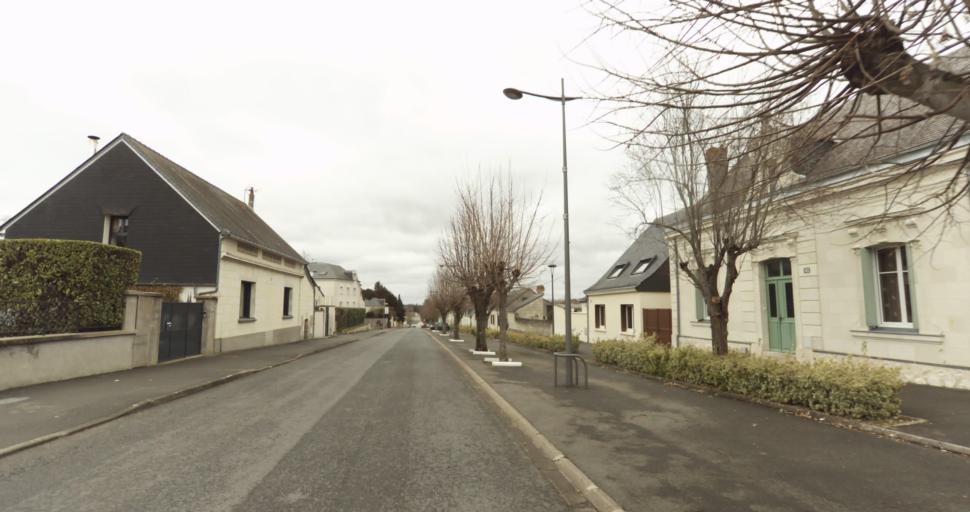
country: FR
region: Pays de la Loire
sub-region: Departement de Maine-et-Loire
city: Jumelles
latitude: 47.3787
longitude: -0.1065
